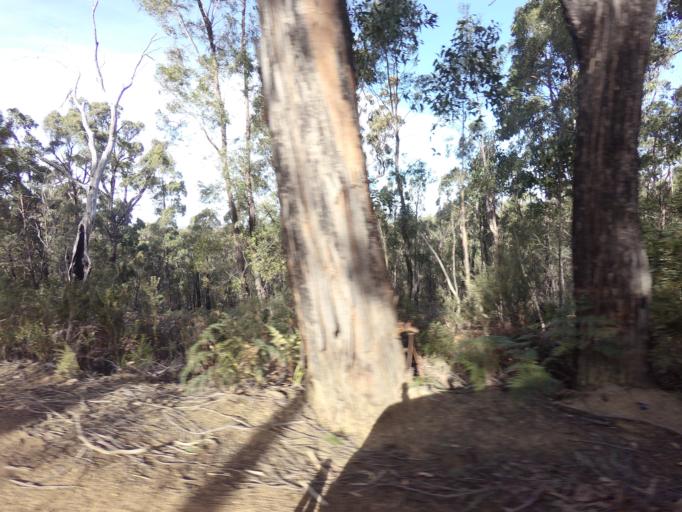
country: AU
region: Tasmania
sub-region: Kingborough
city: Kettering
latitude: -43.0951
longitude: 147.2627
